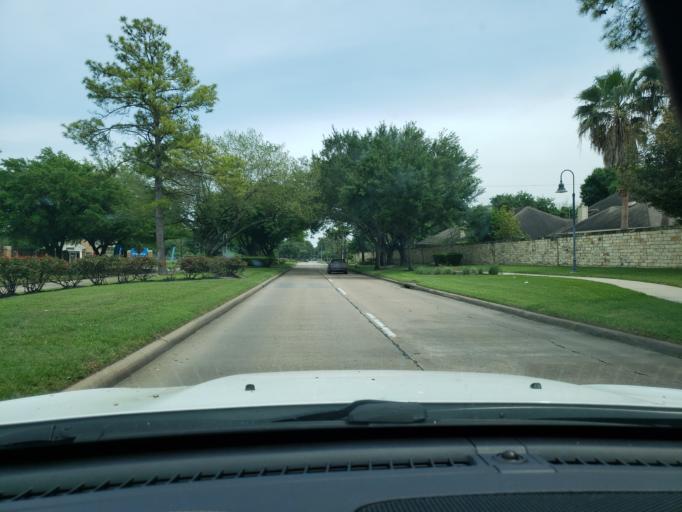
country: US
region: Texas
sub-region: Harris County
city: Jersey Village
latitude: 29.9097
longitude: -95.5796
